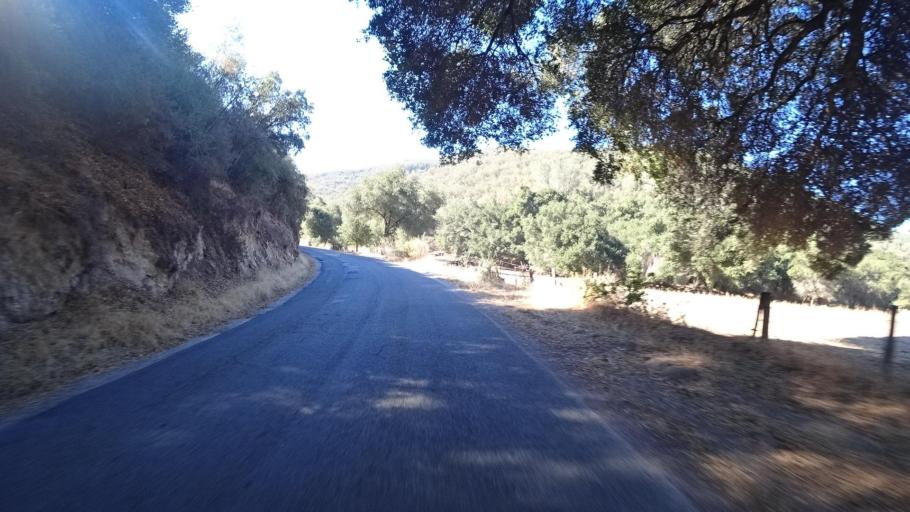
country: US
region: California
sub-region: Monterey County
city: King City
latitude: 36.0402
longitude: -121.0797
